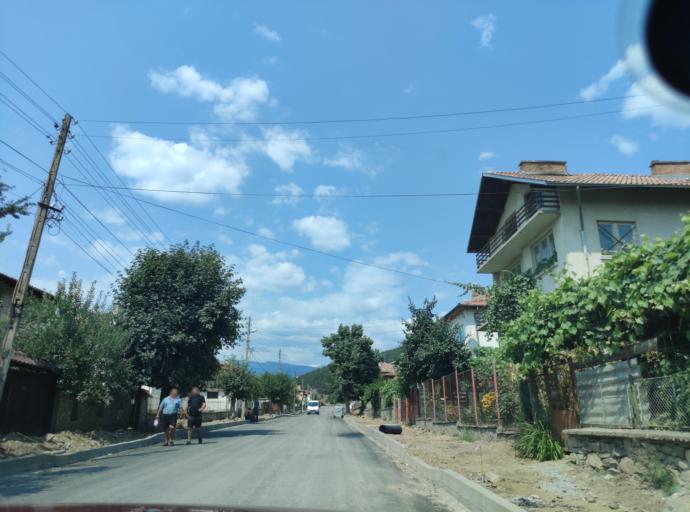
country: BG
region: Blagoevgrad
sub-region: Obshtina Belitsa
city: Belitsa
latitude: 41.9448
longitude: 23.5649
